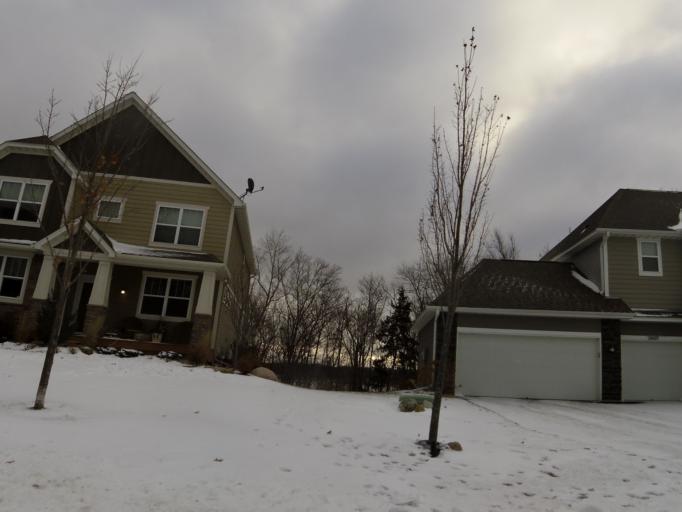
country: US
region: Minnesota
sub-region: Scott County
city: Prior Lake
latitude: 44.6978
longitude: -93.4458
